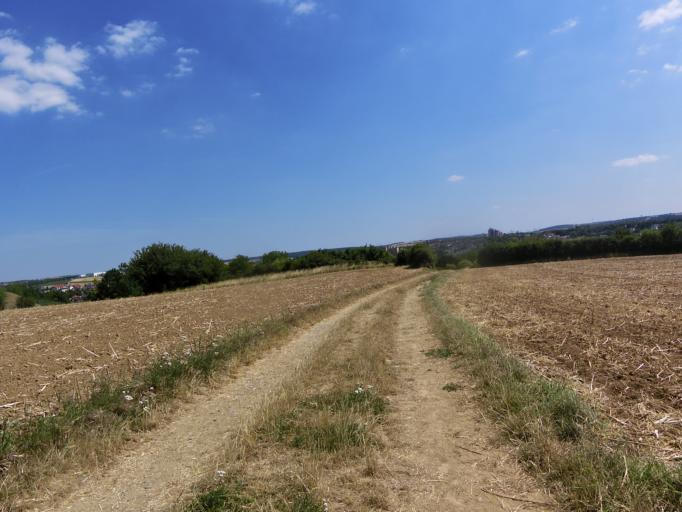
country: DE
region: Bavaria
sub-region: Regierungsbezirk Unterfranken
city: Wuerzburg
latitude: 49.8175
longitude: 9.9571
